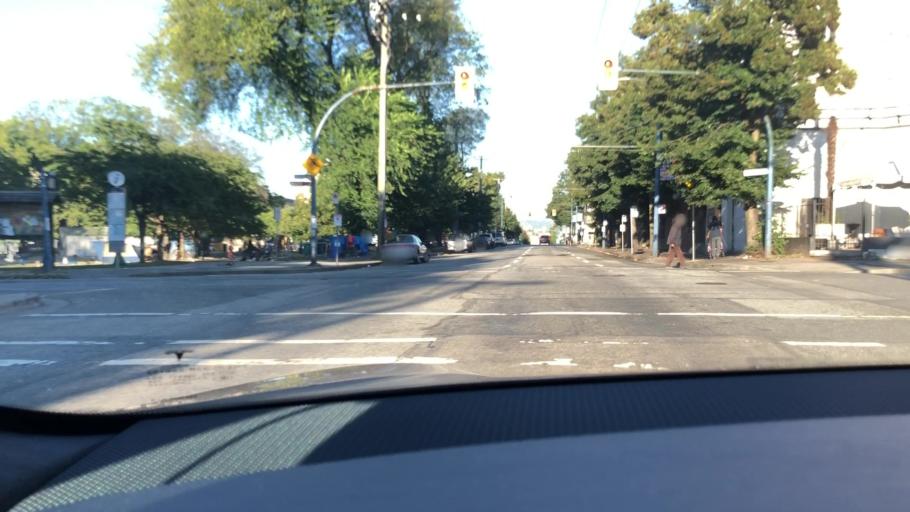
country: CA
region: British Columbia
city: West End
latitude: 49.2822
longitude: -123.0956
